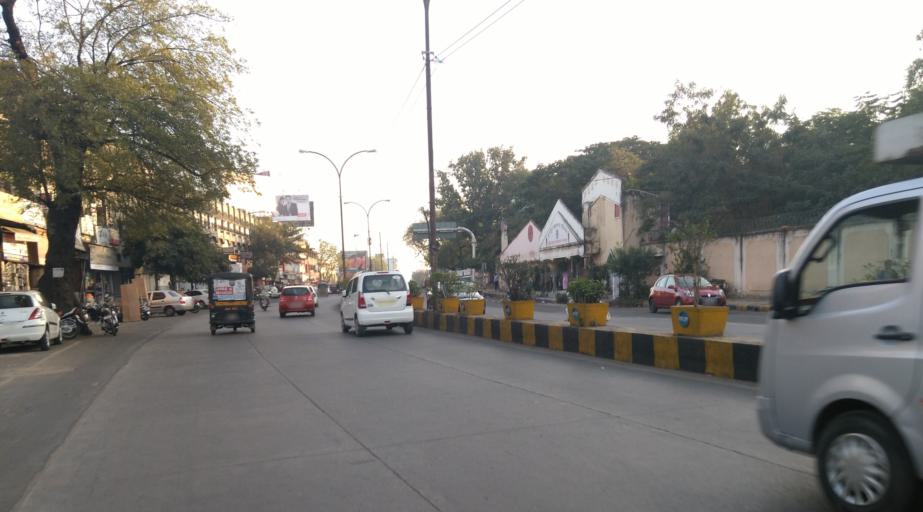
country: IN
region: Maharashtra
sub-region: Nagpur Division
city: Nagpur
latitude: 21.1657
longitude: 79.0795
